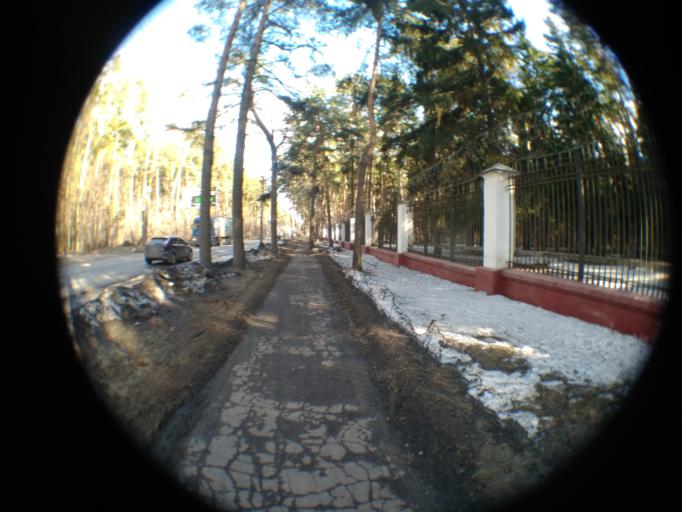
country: RU
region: Moskovskaya
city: Kratovo
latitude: 55.5768
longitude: 38.1612
